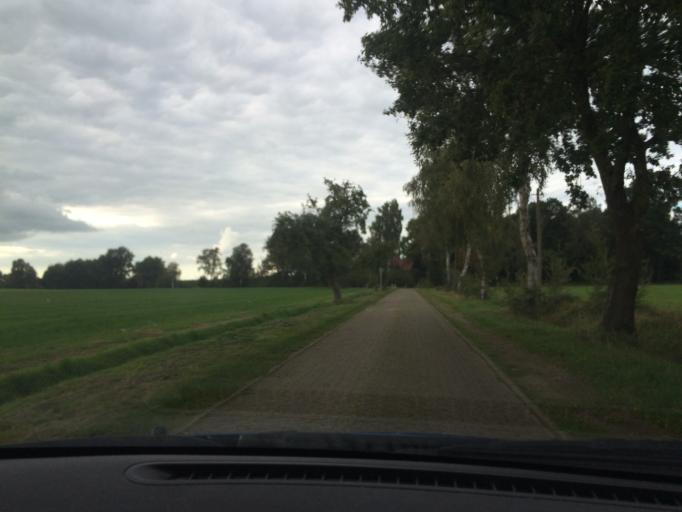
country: DE
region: Lower Saxony
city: Walsrode
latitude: 52.8541
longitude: 9.5486
